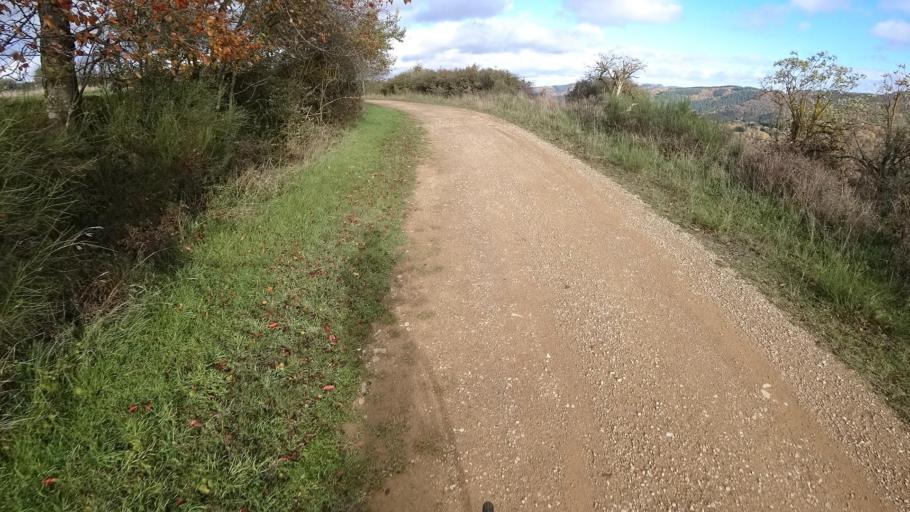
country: DE
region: Rheinland-Pfalz
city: Honningen
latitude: 50.4643
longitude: 6.9402
